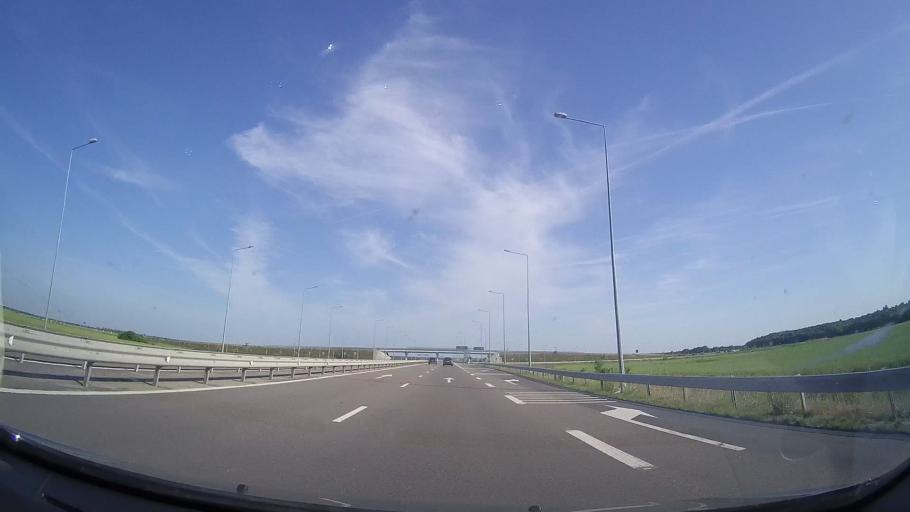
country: RO
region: Prahova
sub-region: Comuna Olari
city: Olari
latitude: 44.7795
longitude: 26.2460
